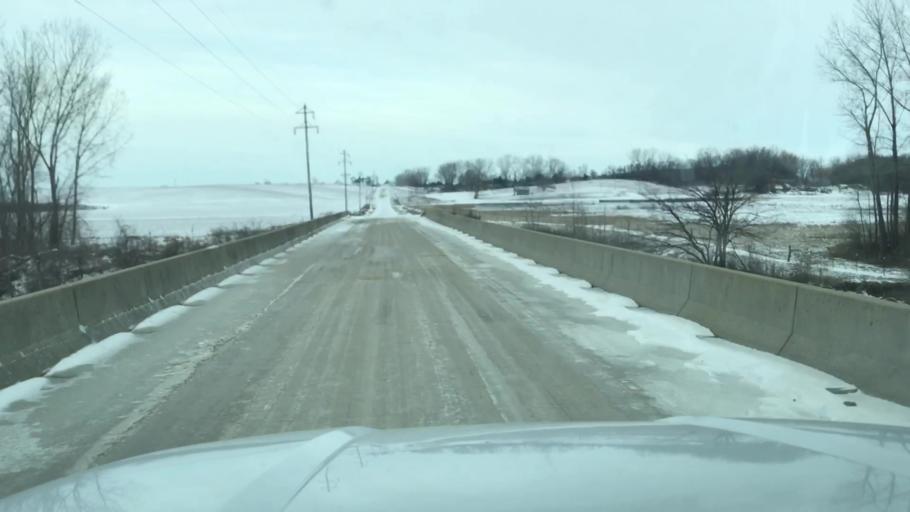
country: US
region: Missouri
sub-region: Holt County
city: Oregon
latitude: 40.1301
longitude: -95.0512
